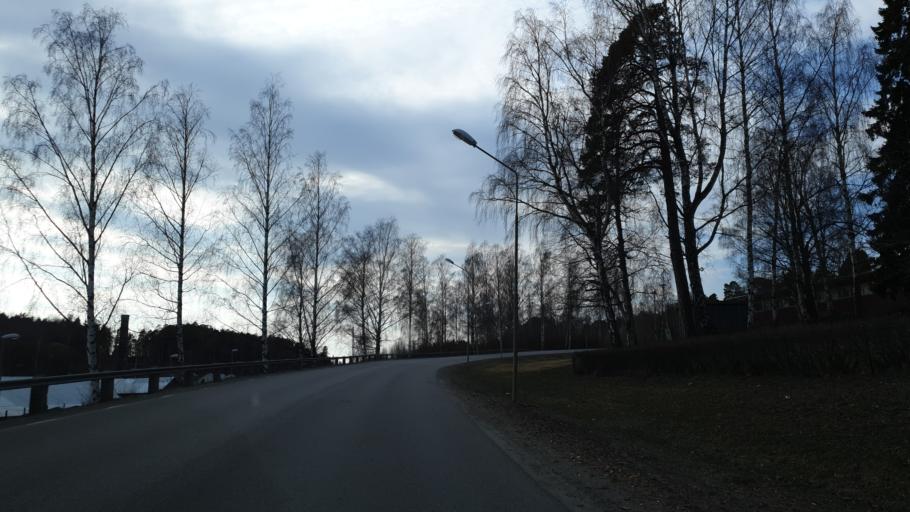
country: SE
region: Gaevleborg
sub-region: Hudiksvalls Kommun
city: Iggesund
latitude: 61.6396
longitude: 17.0763
